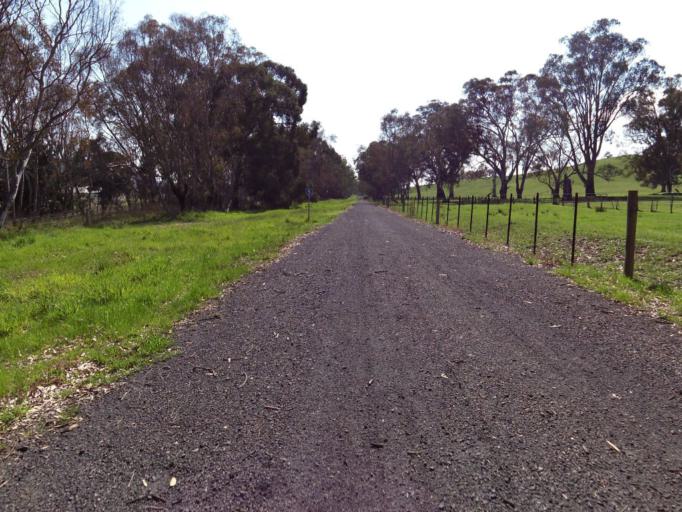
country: AU
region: Victoria
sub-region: Murrindindi
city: Alexandra
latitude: -37.1419
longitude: 145.5893
